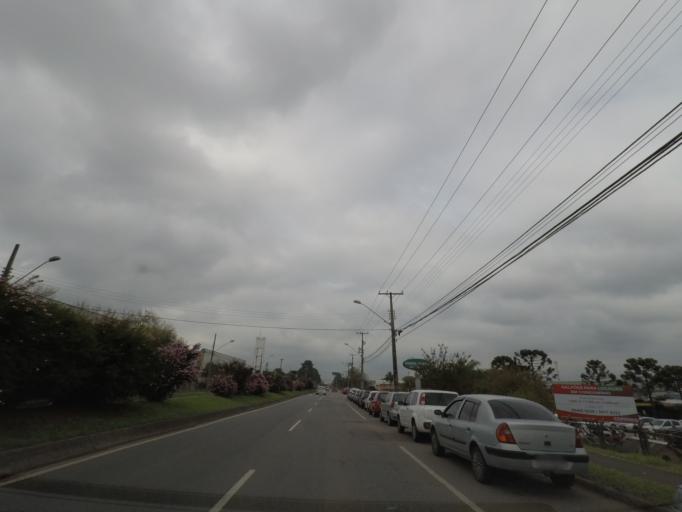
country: BR
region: Parana
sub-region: Curitiba
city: Curitiba
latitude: -25.5001
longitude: -49.3269
